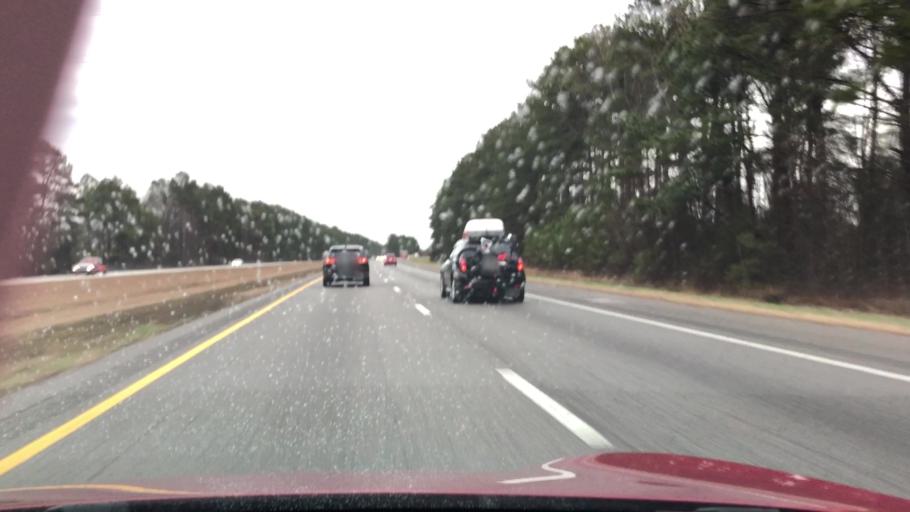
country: US
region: South Carolina
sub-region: Dillon County
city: Latta
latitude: 34.3717
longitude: -79.4896
